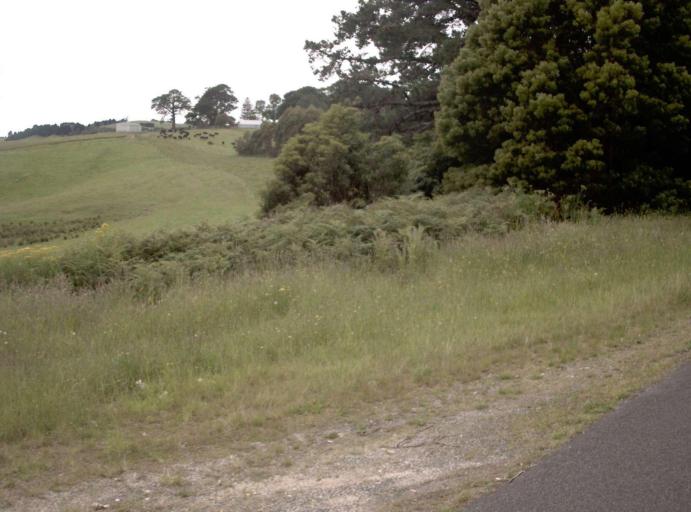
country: AU
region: Victoria
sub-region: Latrobe
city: Moe
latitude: -38.6134
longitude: 146.1364
